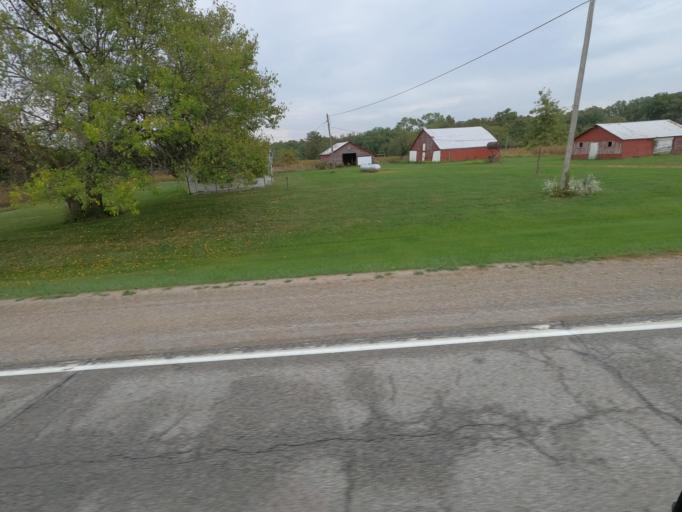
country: US
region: Iowa
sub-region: Van Buren County
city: Keosauqua
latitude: 40.8394
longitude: -92.0087
